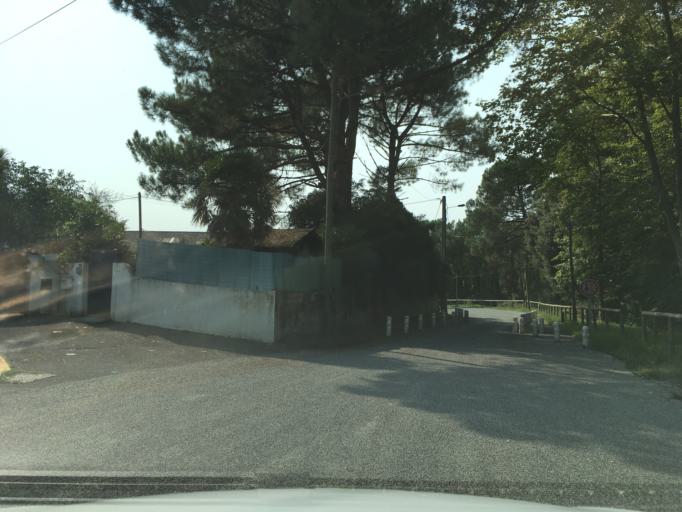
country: FR
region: Aquitaine
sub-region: Departement des Pyrenees-Atlantiques
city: Bayonne
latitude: 43.5143
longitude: -1.4983
